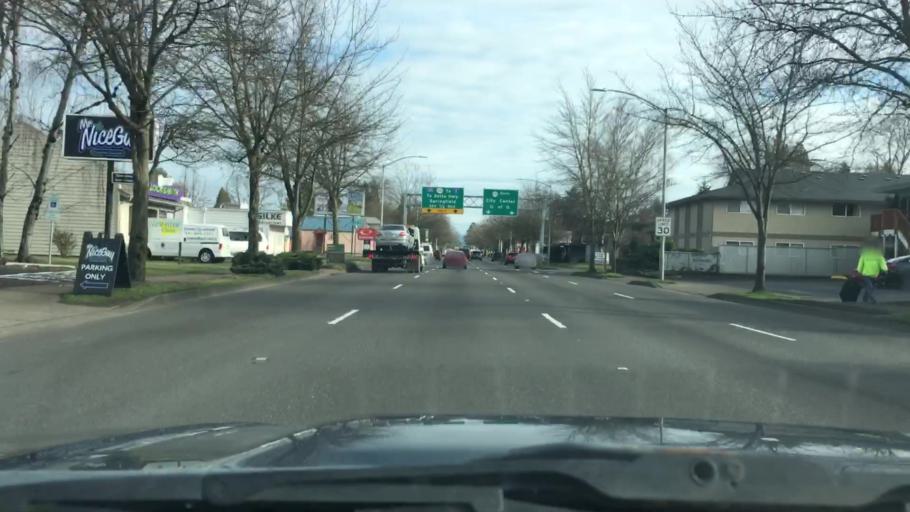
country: US
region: Oregon
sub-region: Lane County
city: Eugene
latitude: 44.0522
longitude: -123.1120
